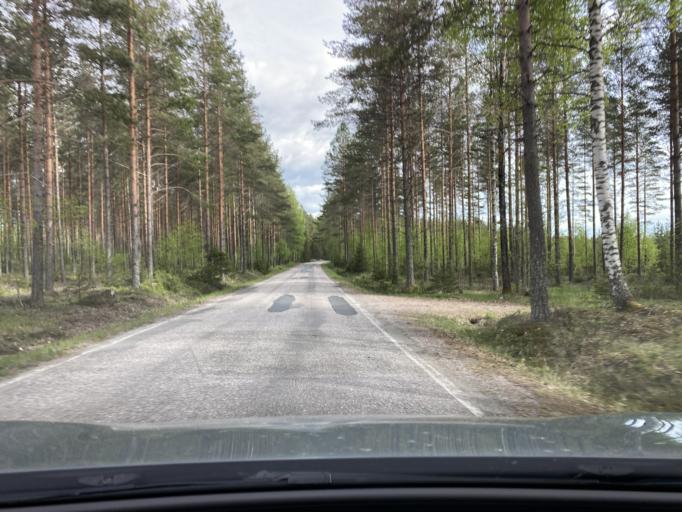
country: FI
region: Varsinais-Suomi
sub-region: Salo
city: Kiikala
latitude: 60.5041
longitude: 23.5451
